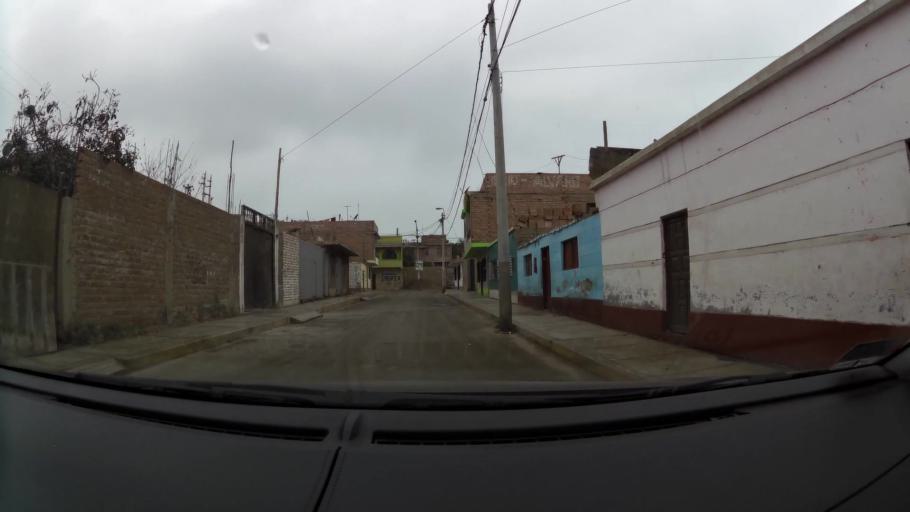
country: PE
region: Lima
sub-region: Provincia de Huaral
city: Chancay
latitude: -11.5875
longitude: -77.2697
